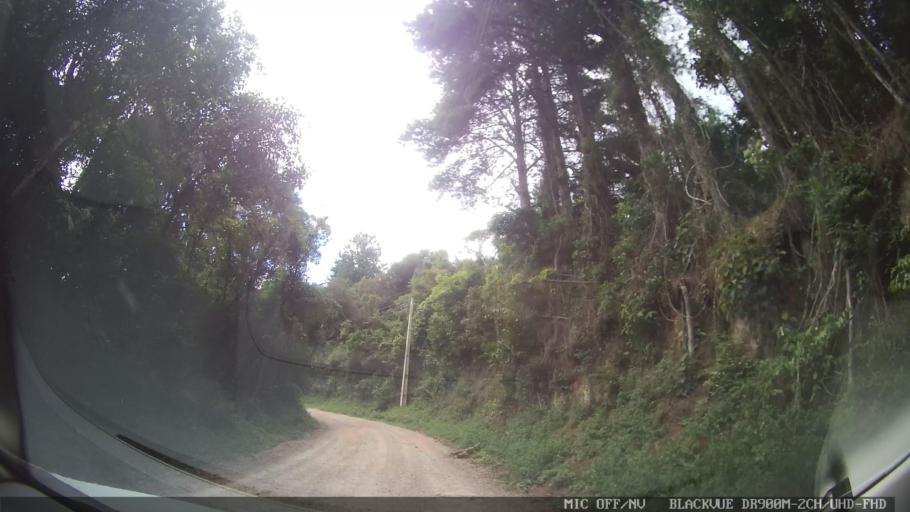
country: BR
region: Minas Gerais
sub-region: Extrema
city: Extrema
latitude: -22.8790
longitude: -46.3172
